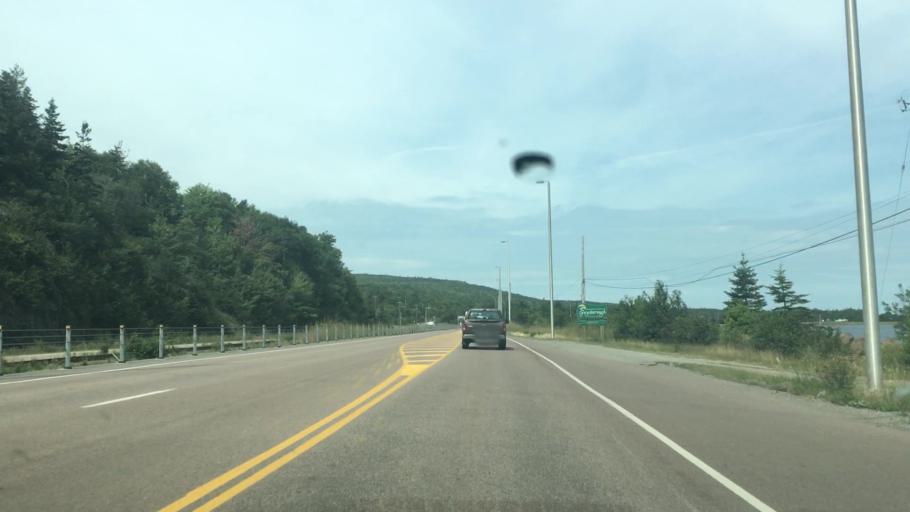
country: CA
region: Nova Scotia
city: Port Hawkesbury
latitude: 45.6427
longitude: -61.4306
